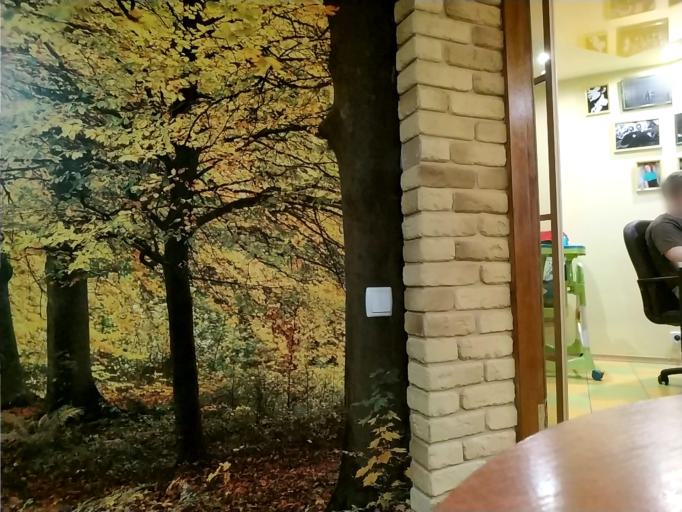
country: RU
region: Tverskaya
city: Zapadnaya Dvina
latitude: 56.3309
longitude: 31.8879
